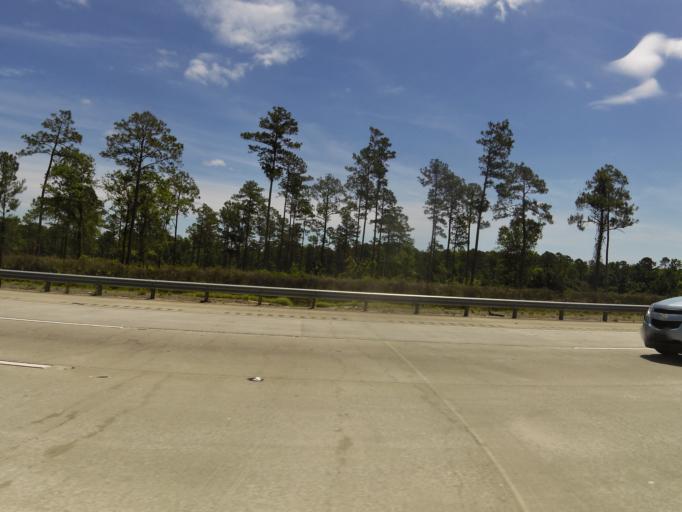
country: US
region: Georgia
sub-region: Glynn County
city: Country Club Estates
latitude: 31.2869
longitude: -81.4861
